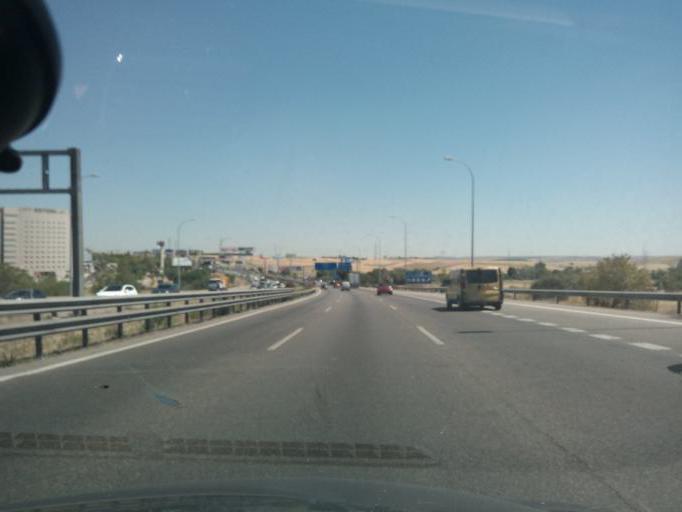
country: ES
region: Madrid
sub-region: Provincia de Madrid
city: San Sebastian de los Reyes
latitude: 40.5352
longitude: -3.6134
